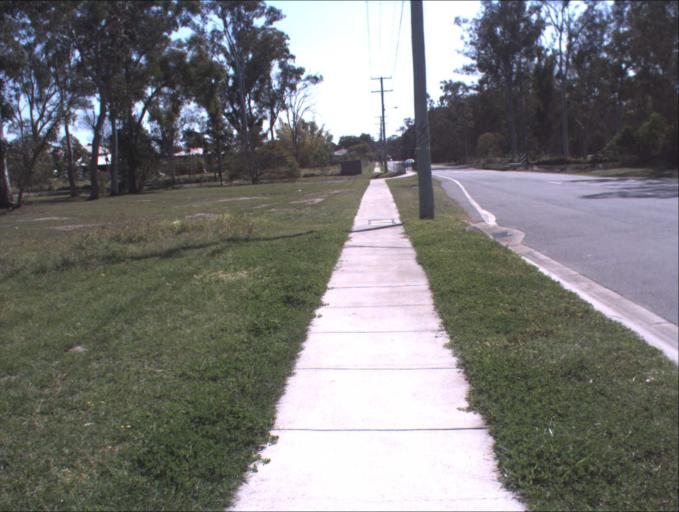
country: AU
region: Queensland
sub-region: Logan
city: Logan City
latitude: -27.6728
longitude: 153.0945
